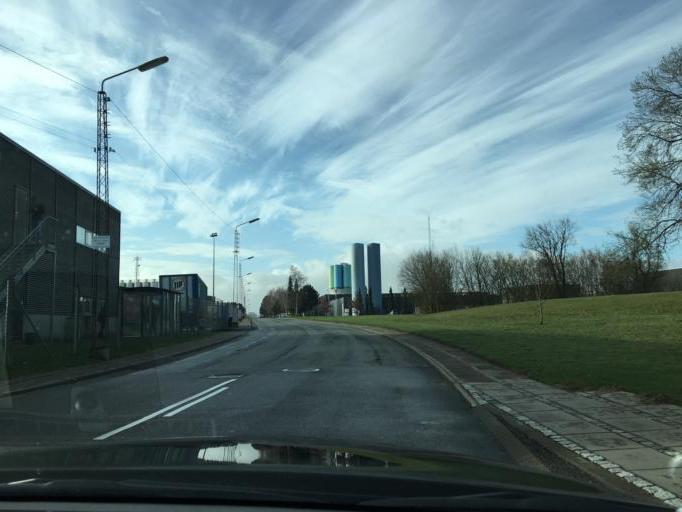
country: DK
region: South Denmark
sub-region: Kolding Kommune
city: Kolding
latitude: 55.5078
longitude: 9.4599
